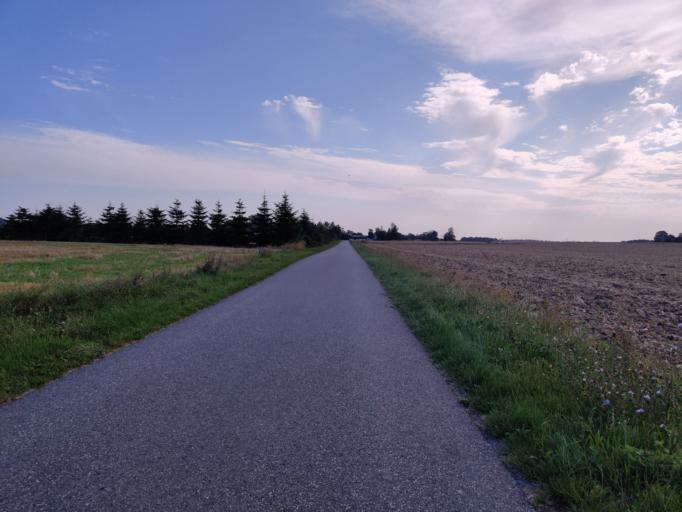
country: DK
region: Zealand
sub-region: Guldborgsund Kommune
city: Nykobing Falster
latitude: 54.7003
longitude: 11.9311
